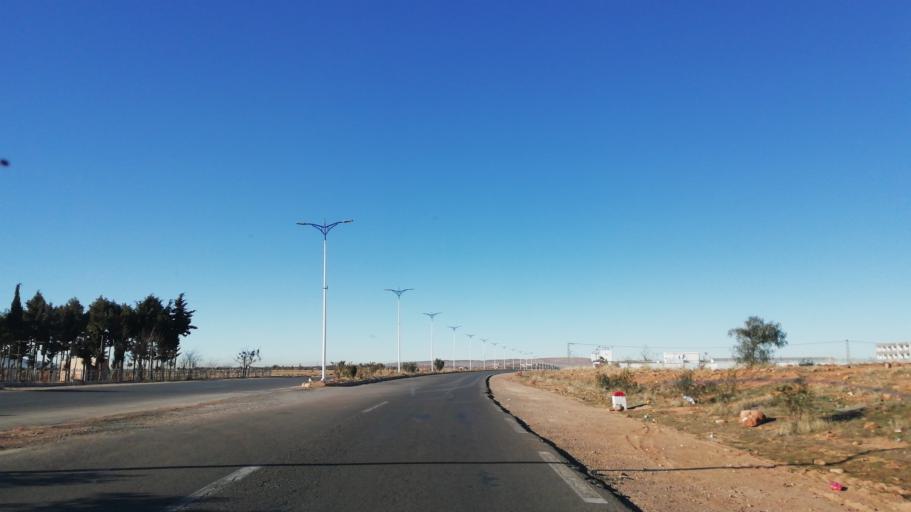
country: DZ
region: El Bayadh
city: El Bayadh
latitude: 33.6918
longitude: 1.0766
